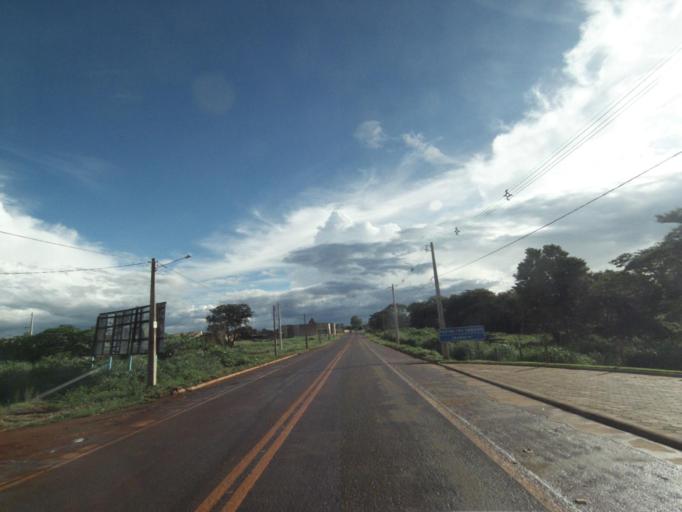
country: BR
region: Goias
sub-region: Itaberai
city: Itaberai
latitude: -16.0370
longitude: -49.7850
